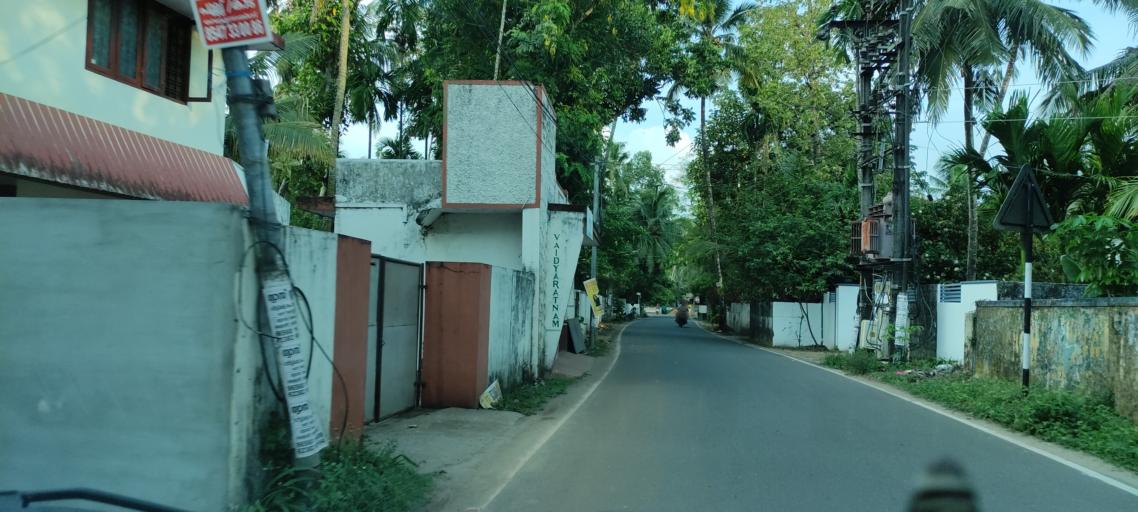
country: IN
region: Kerala
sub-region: Alappuzha
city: Arukutti
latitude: 9.8965
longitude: 76.3089
